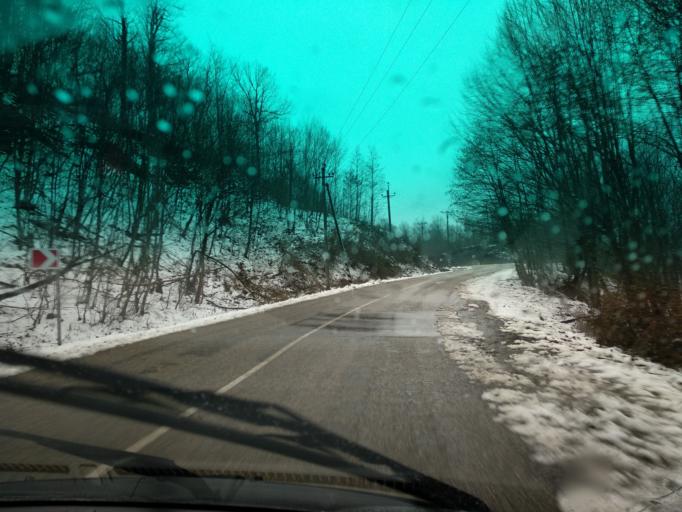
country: RU
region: Krasnodarskiy
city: Khadyzhensk
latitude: 44.2103
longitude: 39.4137
